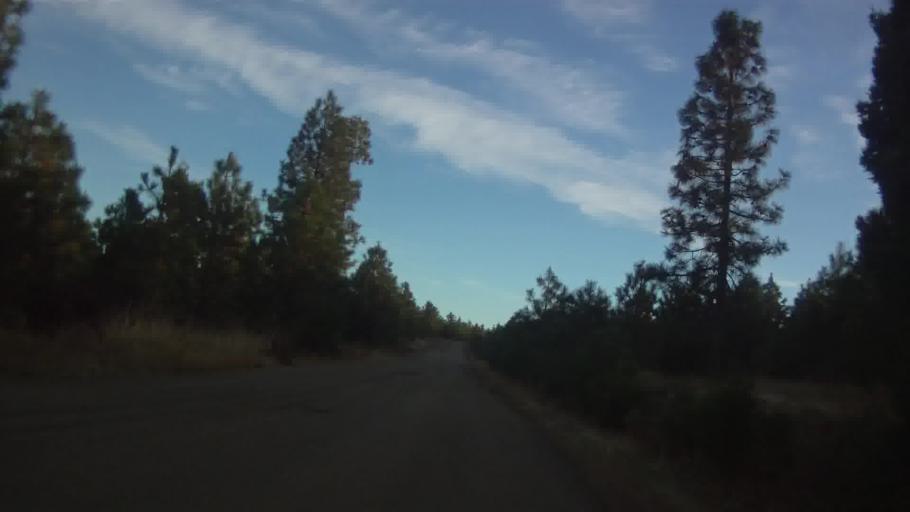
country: US
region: California
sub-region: Shasta County
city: Shingletown
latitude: 40.6299
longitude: -121.8575
